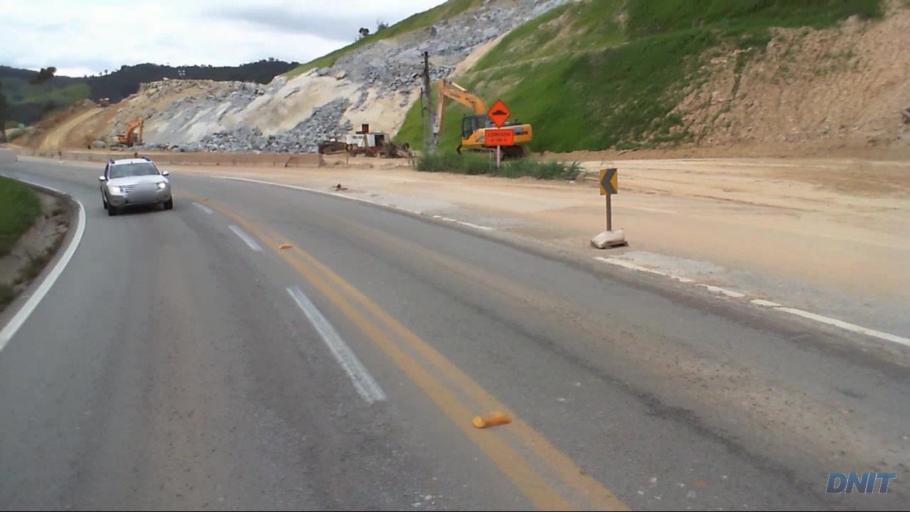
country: BR
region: Minas Gerais
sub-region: Caete
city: Caete
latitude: -19.7861
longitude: -43.6692
